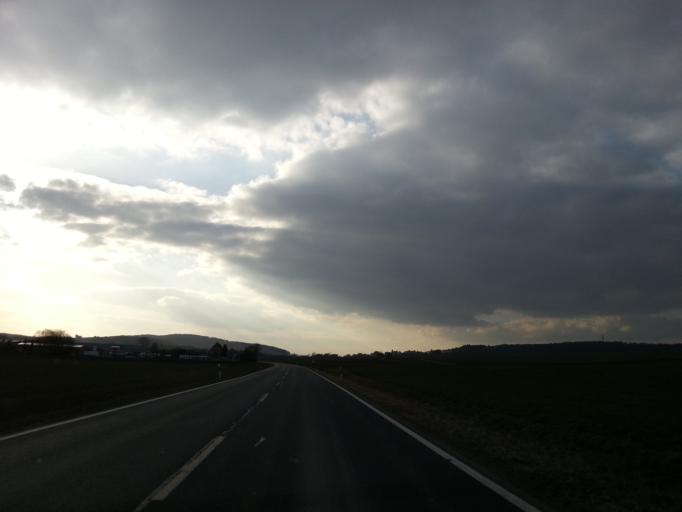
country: DE
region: Bavaria
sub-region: Regierungsbezirk Unterfranken
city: Helmstadt
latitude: 49.7599
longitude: 9.7381
